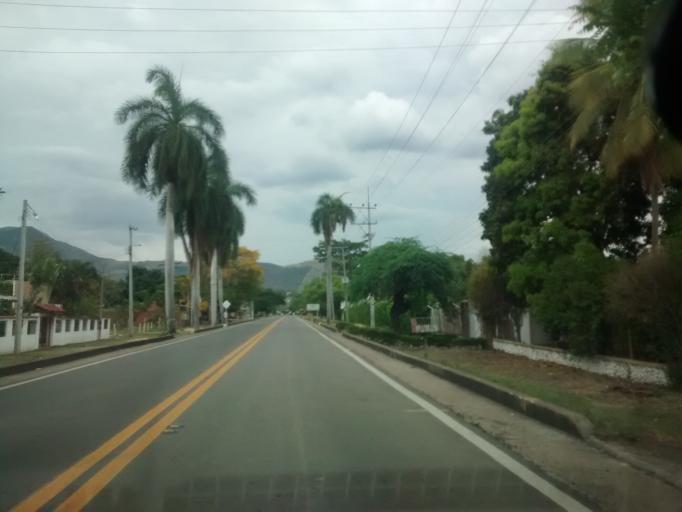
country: CO
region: Cundinamarca
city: Tocaima
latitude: 4.4526
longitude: -74.6486
